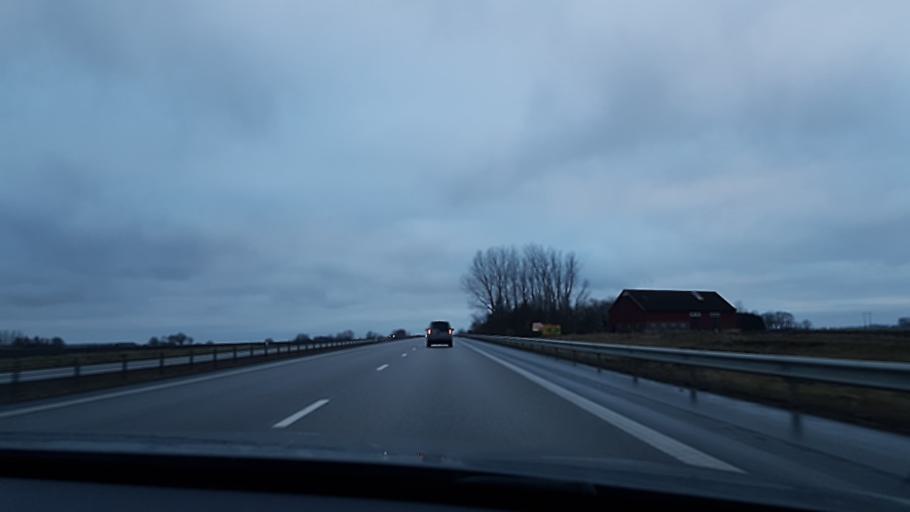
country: SE
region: Skane
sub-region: Astorps Kommun
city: Astorp
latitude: 56.1751
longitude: 12.9979
